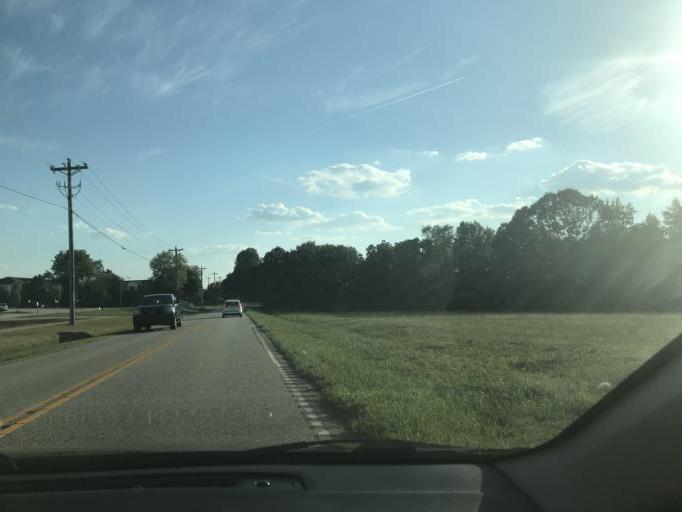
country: US
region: South Carolina
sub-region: Cherokee County
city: Gaffney
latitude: 35.1016
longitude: -81.6882
